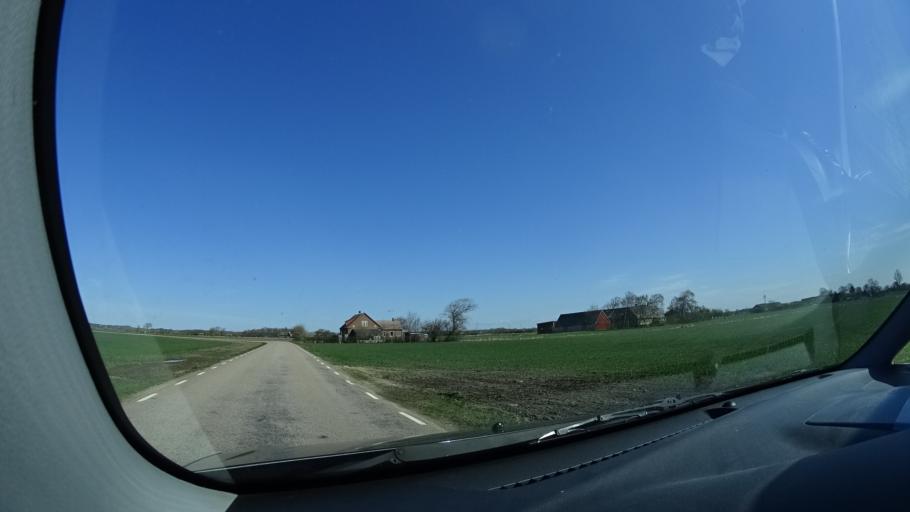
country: SE
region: Skane
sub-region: Hoganas Kommun
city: Hoganas
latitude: 56.2236
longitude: 12.5926
